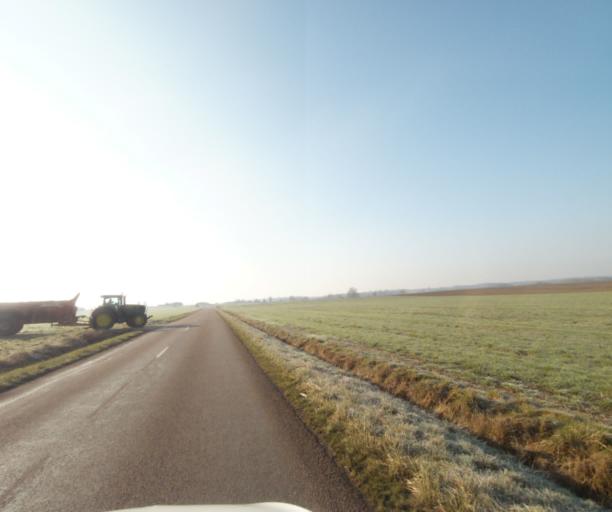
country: FR
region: Champagne-Ardenne
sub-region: Departement de la Haute-Marne
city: Montier-en-Der
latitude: 48.4197
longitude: 4.7446
